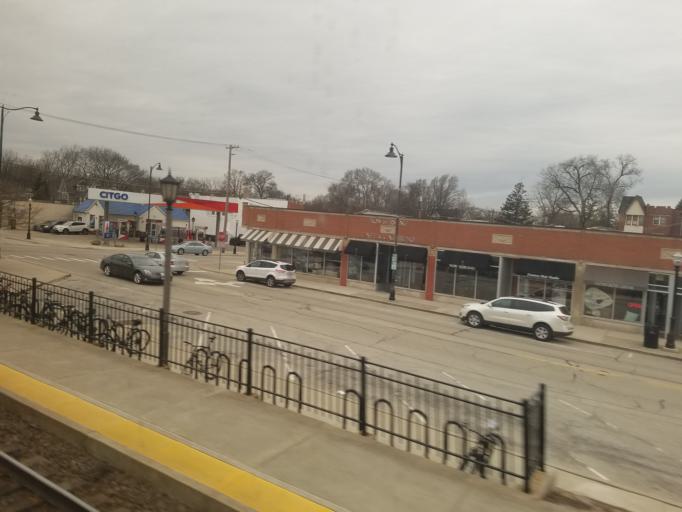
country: US
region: Illinois
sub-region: Cook County
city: La Grange
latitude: 41.8143
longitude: -87.8773
